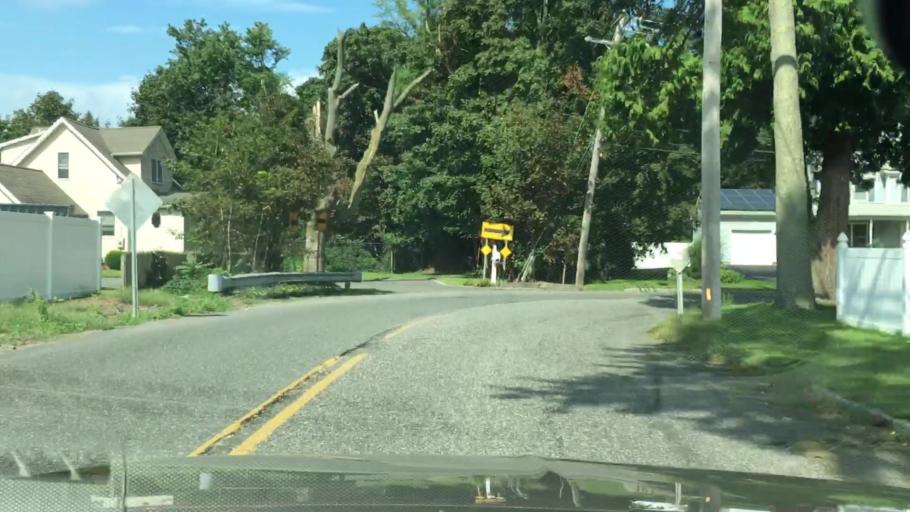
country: US
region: New York
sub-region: Suffolk County
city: Ronkonkoma
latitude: 40.8004
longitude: -73.1264
